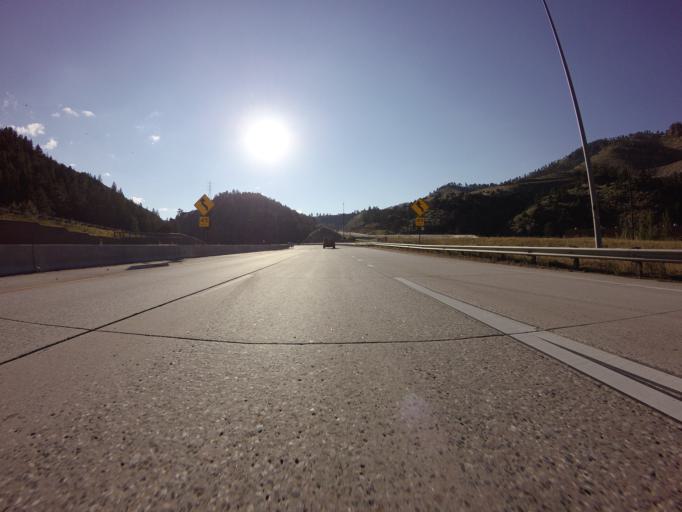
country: US
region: Colorado
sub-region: Clear Creek County
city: Idaho Springs
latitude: 39.7473
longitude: -105.4632
